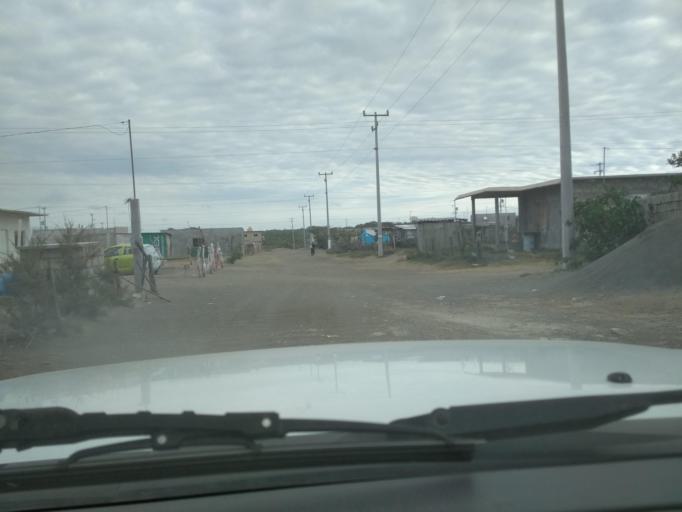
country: MX
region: Veracruz
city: Anton Lizardo
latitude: 19.0457
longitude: -95.9927
